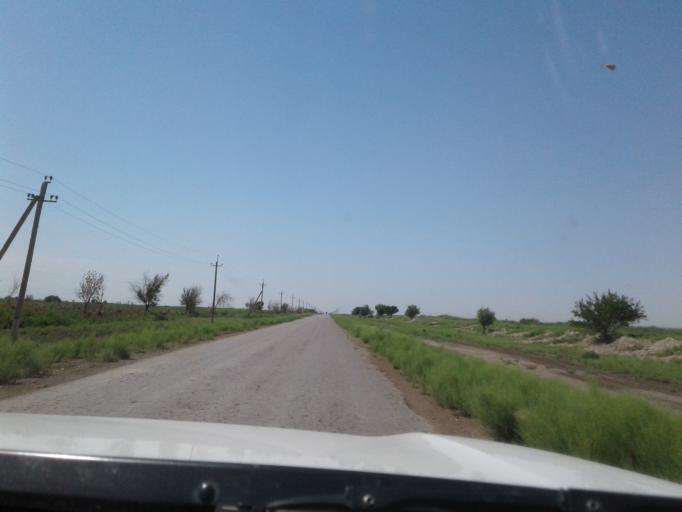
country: TM
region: Dasoguz
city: Koeneuergench
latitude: 41.8508
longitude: 58.7050
